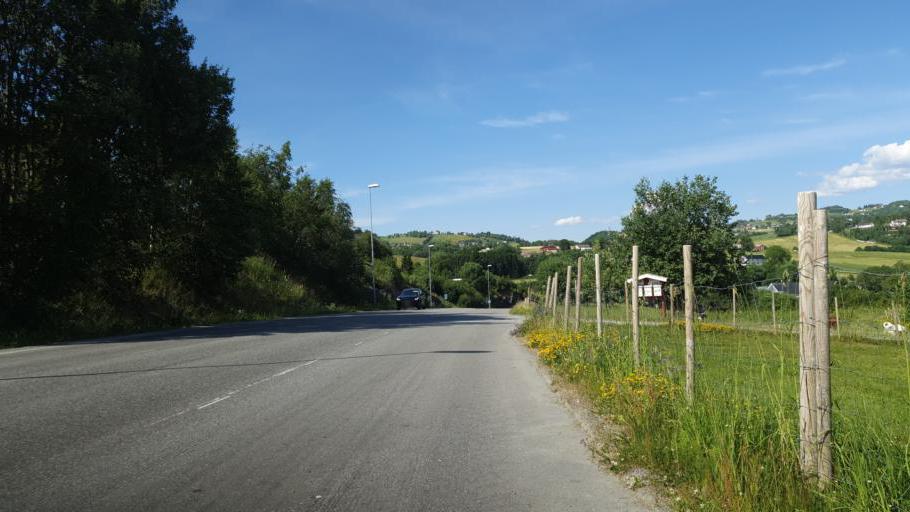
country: NO
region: Nord-Trondelag
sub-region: Leksvik
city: Leksvik
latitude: 63.6657
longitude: 10.6072
